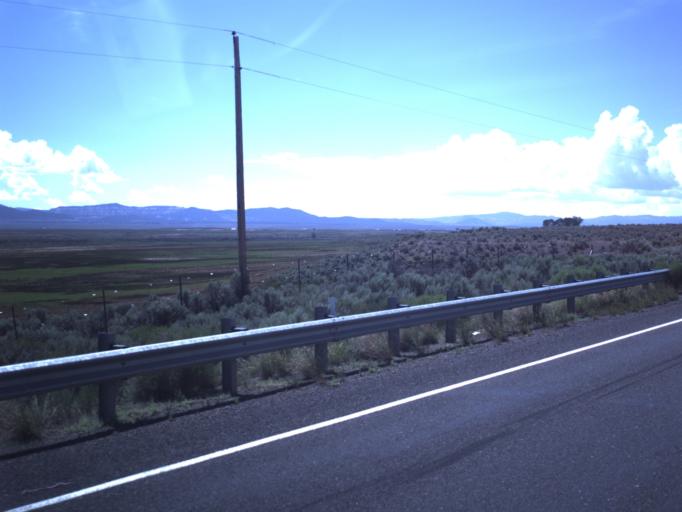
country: US
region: Utah
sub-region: Garfield County
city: Panguitch
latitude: 37.9264
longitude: -112.4270
